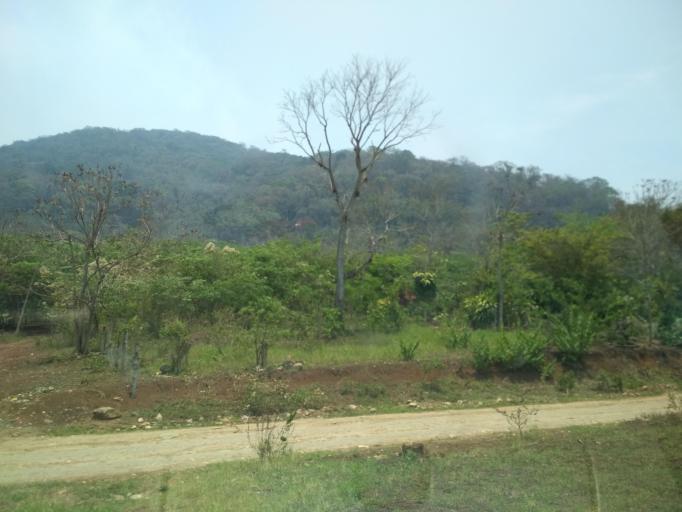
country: MX
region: Veracruz
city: Cosolapa
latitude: 18.5916
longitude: -96.6973
